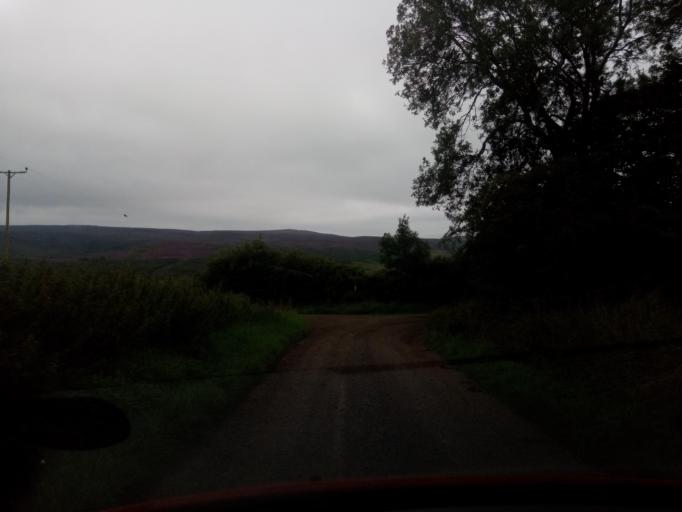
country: GB
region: England
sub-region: Northumberland
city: Otterburn
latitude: 55.2751
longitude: -2.0896
